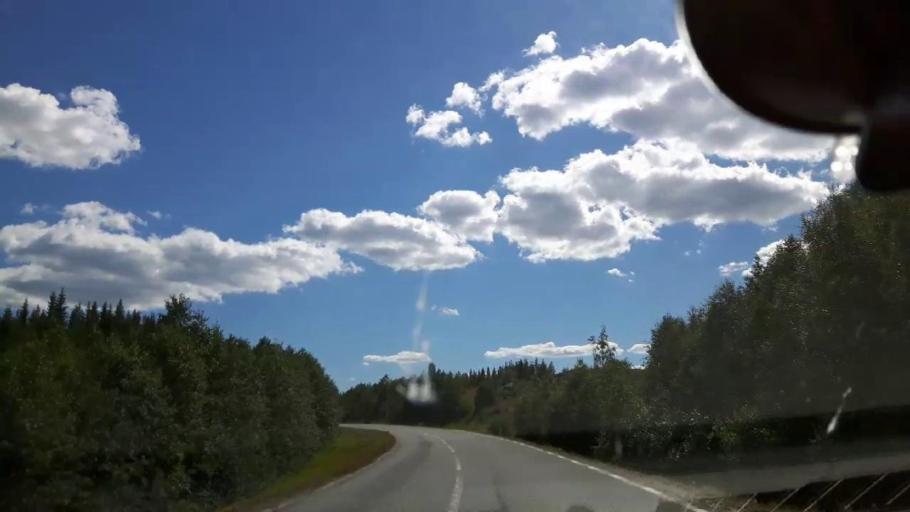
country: SE
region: Jaemtland
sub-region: Ragunda Kommun
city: Hammarstrand
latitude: 62.8666
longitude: 16.2135
